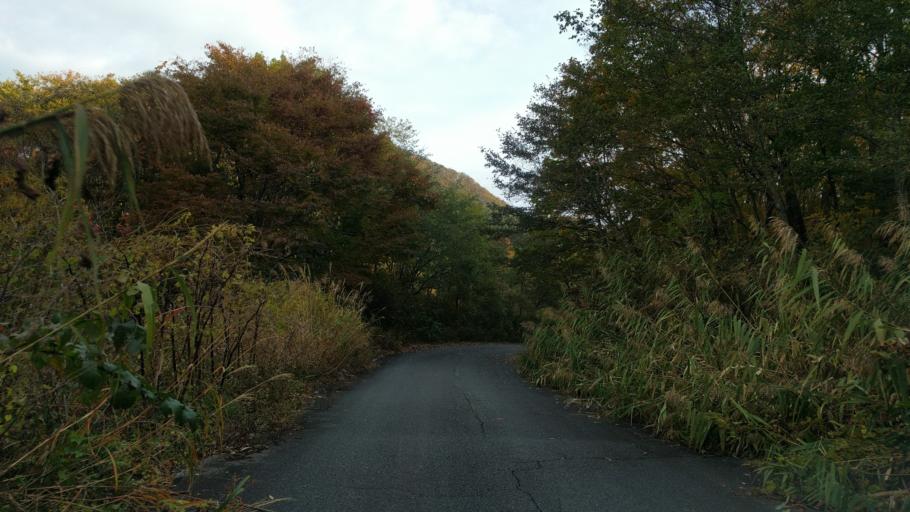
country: JP
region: Fukushima
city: Kitakata
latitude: 37.3970
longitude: 139.7487
